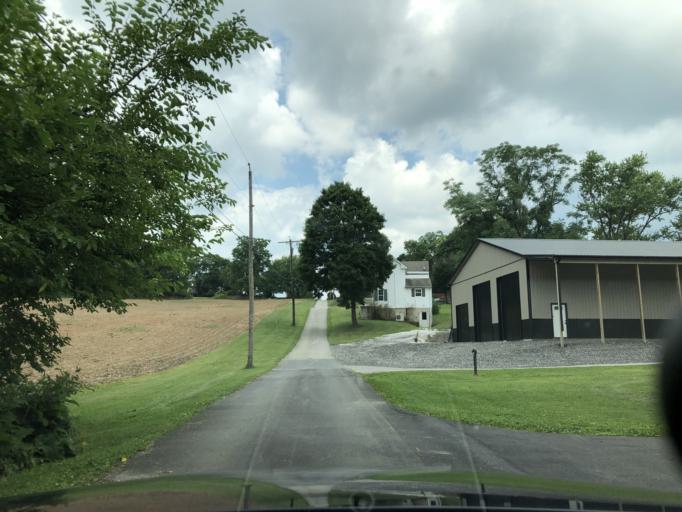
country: US
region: Maryland
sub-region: Carroll County
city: Westminster
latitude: 39.5482
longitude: -76.9888
